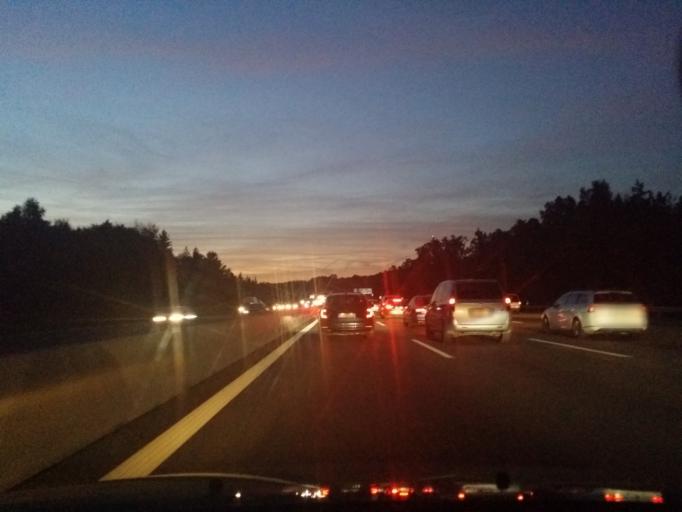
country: DE
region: Baden-Wuerttemberg
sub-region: Regierungsbezirk Stuttgart
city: Schonaich
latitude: 48.7208
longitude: 9.0782
